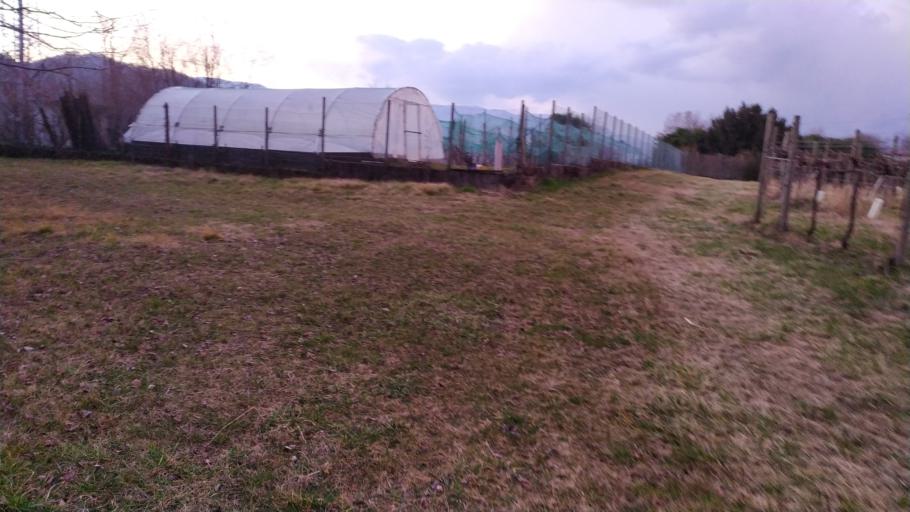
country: IT
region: Veneto
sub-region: Provincia di Treviso
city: Cornuda
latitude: 45.8386
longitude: 11.9965
